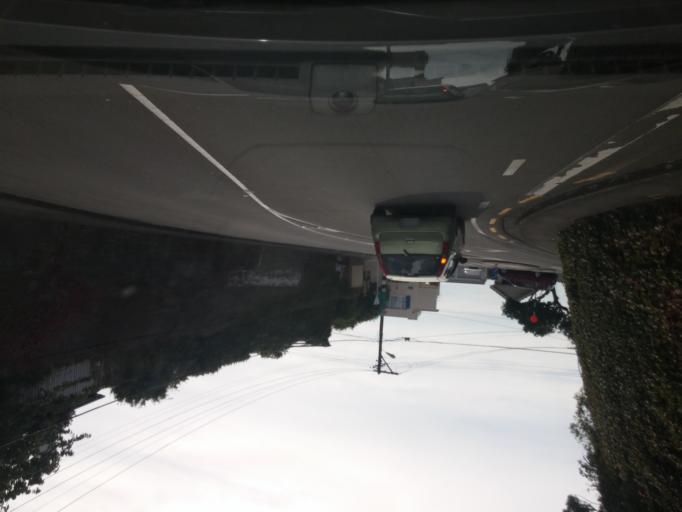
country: NZ
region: Wellington
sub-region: Wellington City
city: Kelburn
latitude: -41.2872
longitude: 174.7667
